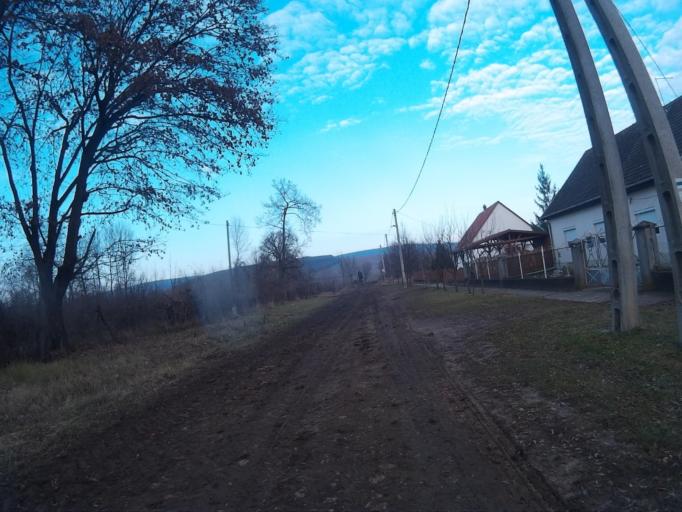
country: HU
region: Nograd
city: Bercel
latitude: 47.9825
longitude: 19.4247
